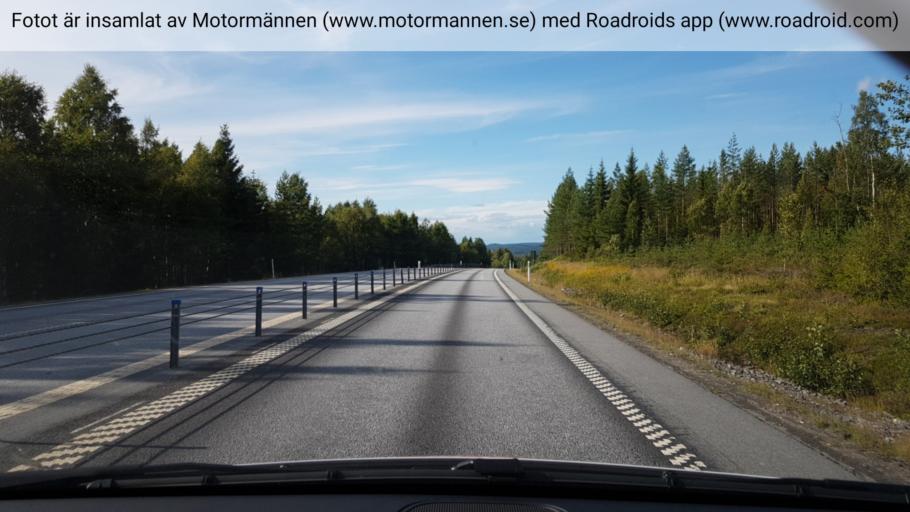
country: SE
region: Vaesterbotten
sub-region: Vannas Kommun
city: Vannasby
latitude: 63.9049
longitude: 19.8928
